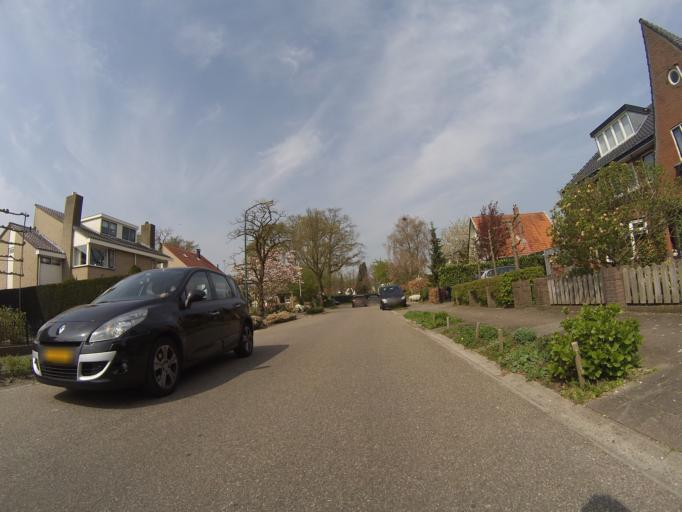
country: NL
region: Utrecht
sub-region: Gemeente Soest
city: Soest
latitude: 52.1671
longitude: 5.3130
